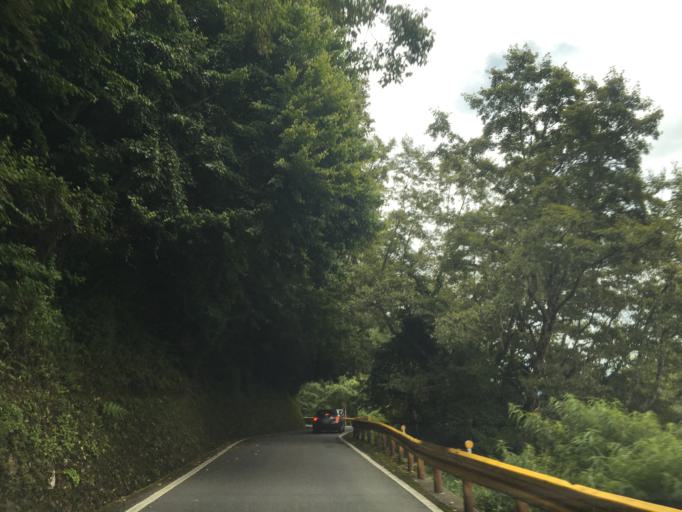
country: TW
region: Taiwan
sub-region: Hualien
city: Hualian
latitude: 24.1732
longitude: 121.3805
